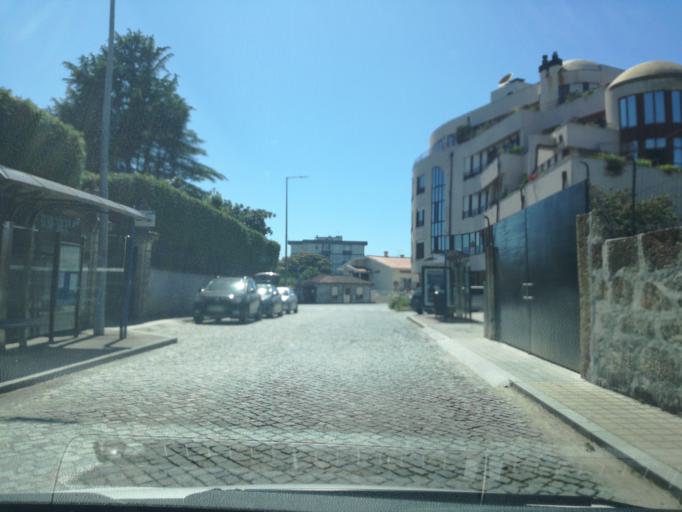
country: PT
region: Porto
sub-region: Maia
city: Maia
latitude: 41.2303
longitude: -8.6190
